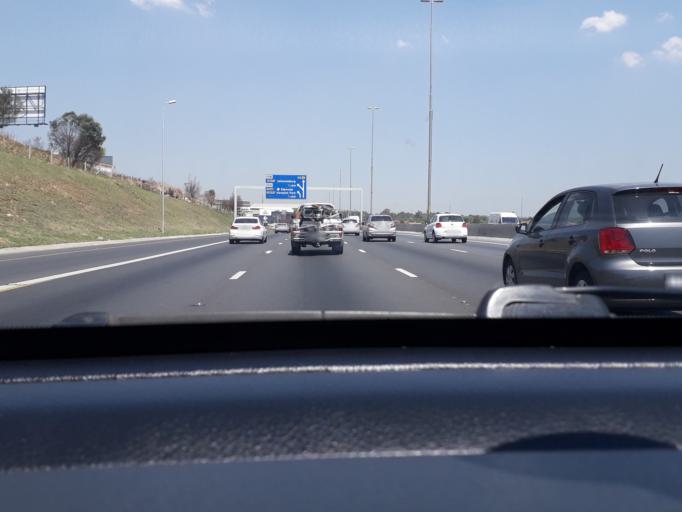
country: ZA
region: Gauteng
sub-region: City of Johannesburg Metropolitan Municipality
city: Modderfontein
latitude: -26.1055
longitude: 28.1259
